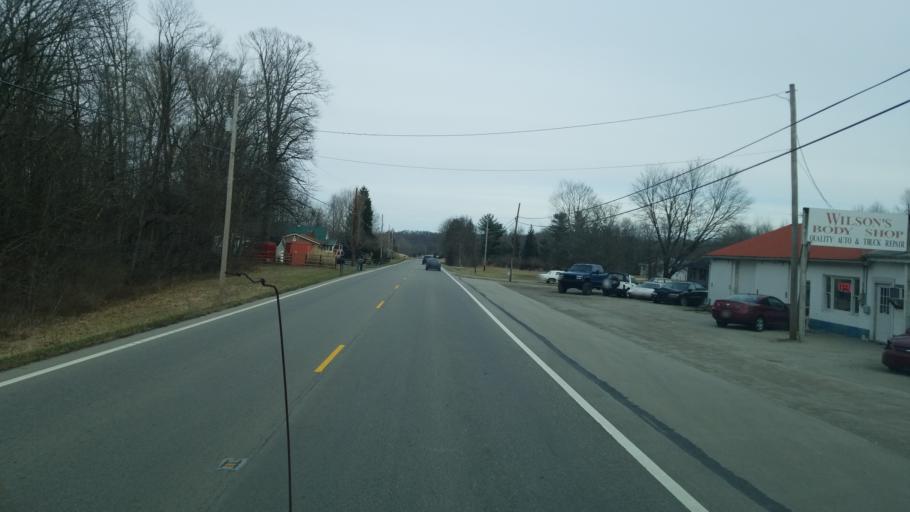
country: US
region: Ohio
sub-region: Highland County
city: Hillsboro
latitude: 39.1538
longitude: -83.6586
